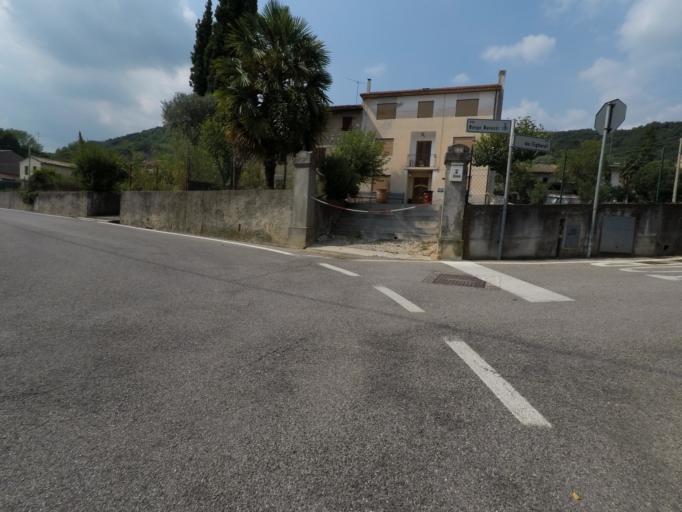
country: IT
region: Friuli Venezia Giulia
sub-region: Provincia di Pordenone
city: Caneva
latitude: 45.9682
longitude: 12.4298
